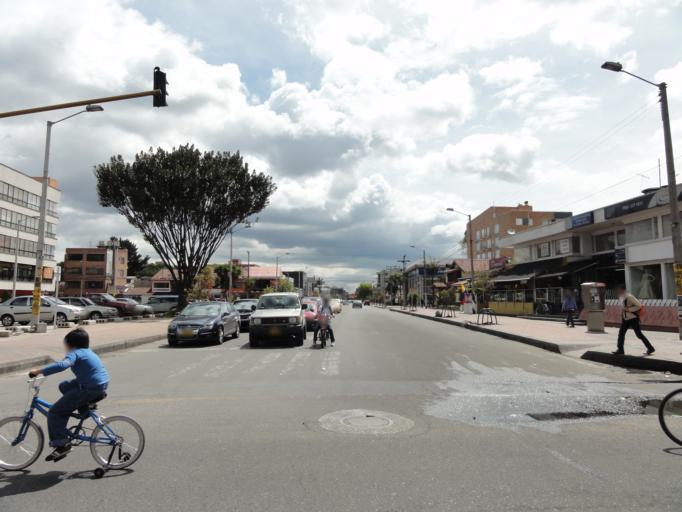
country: CO
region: Bogota D.C.
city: Barrio San Luis
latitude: 4.7008
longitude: -74.0430
